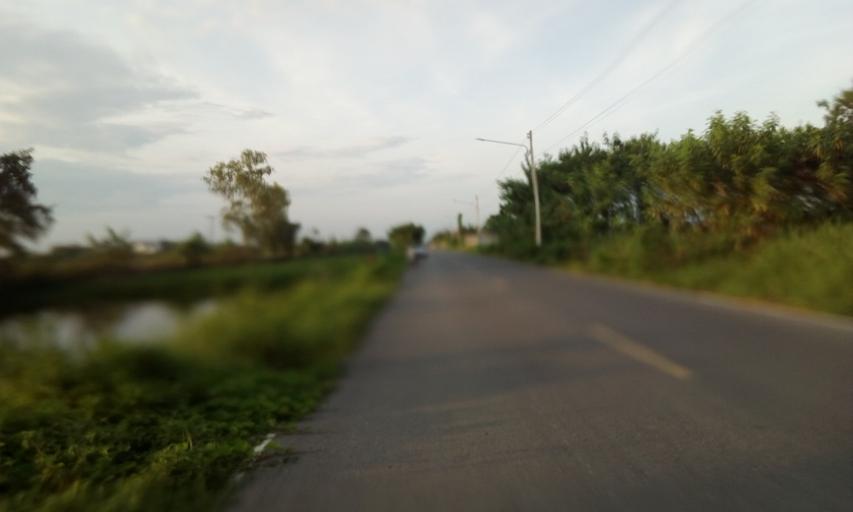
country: TH
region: Pathum Thani
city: Nong Suea
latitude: 14.0473
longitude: 100.8463
